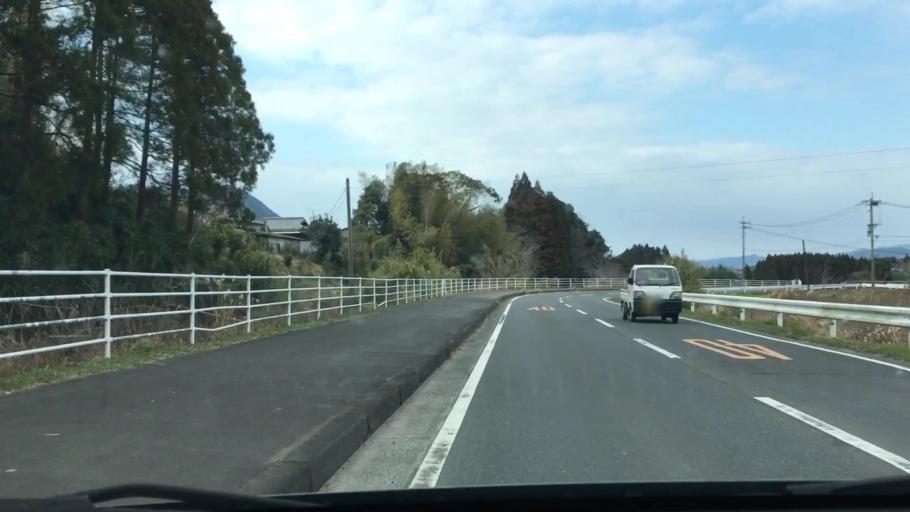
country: JP
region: Miyazaki
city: Kushima
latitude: 31.4981
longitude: 131.2388
